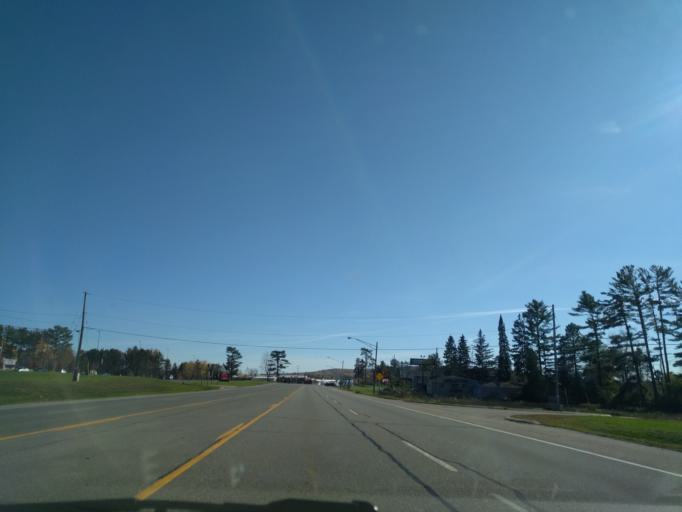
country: US
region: Michigan
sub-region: Dickinson County
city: Iron Mountain
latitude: 45.8482
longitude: -88.0512
